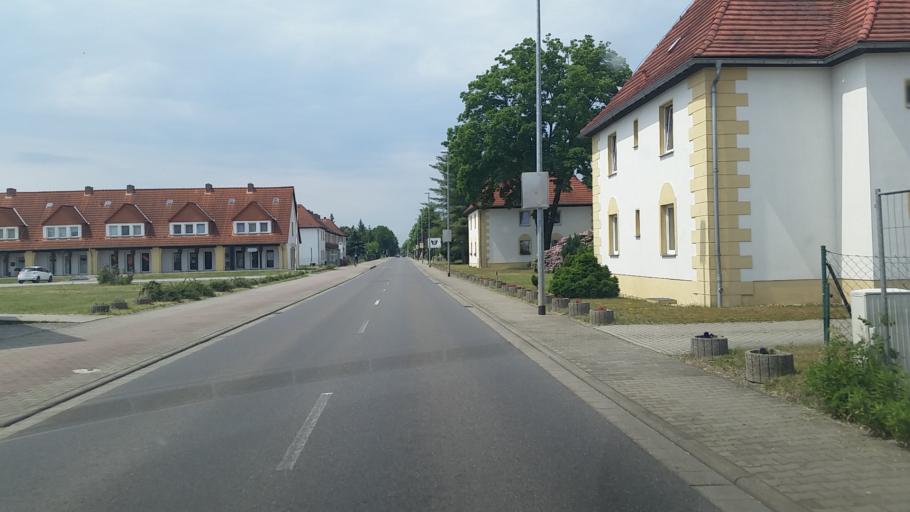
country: DE
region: Brandenburg
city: Schwarzheide
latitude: 51.4800
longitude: 13.8494
